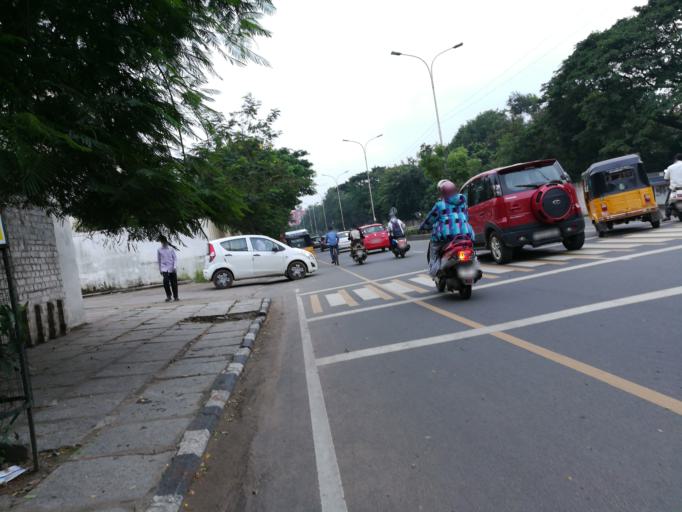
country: IN
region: Tamil Nadu
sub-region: Chennai
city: Gandhi Nagar
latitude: 13.0158
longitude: 80.2406
